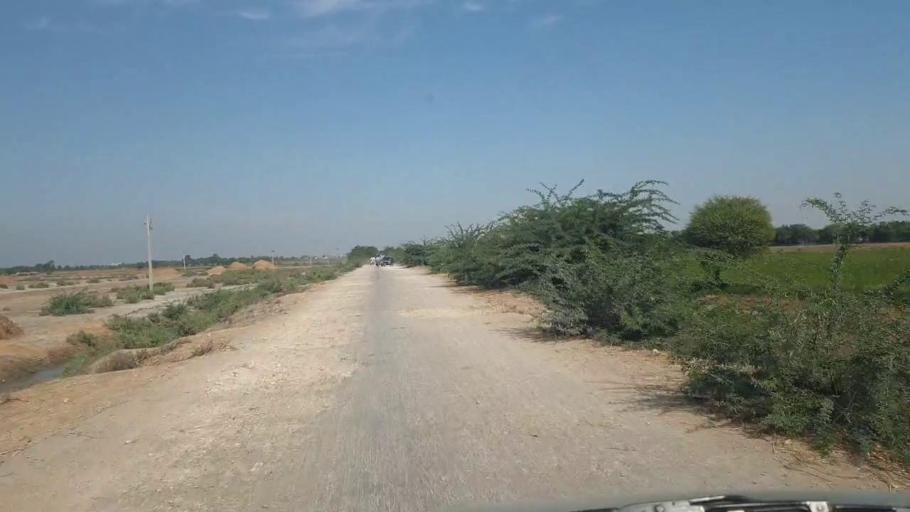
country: PK
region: Sindh
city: Tando Bago
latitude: 24.8804
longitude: 69.0007
